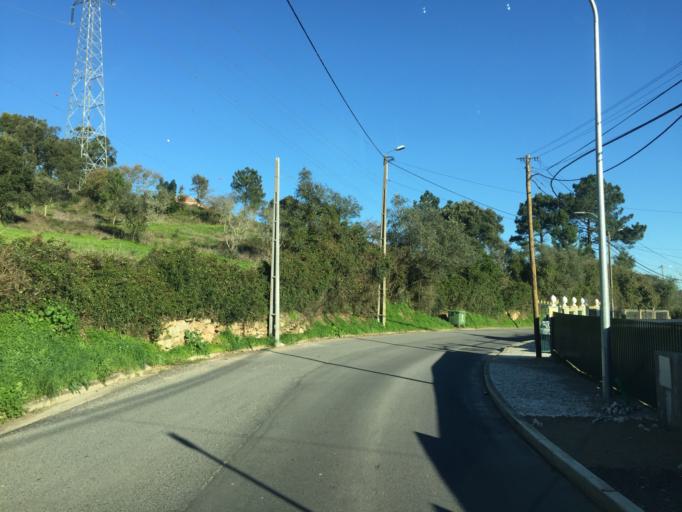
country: PT
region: Lisbon
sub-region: Odivelas
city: Canecas
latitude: 38.8213
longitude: -9.2353
